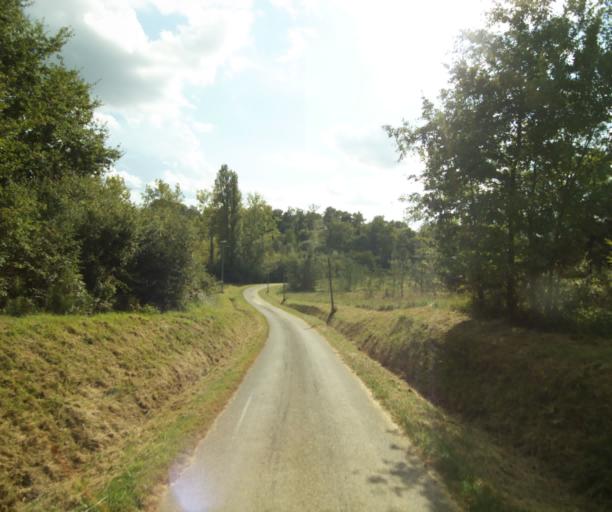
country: FR
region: Midi-Pyrenees
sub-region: Departement du Gers
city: Cazaubon
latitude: 43.9237
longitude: -0.0486
